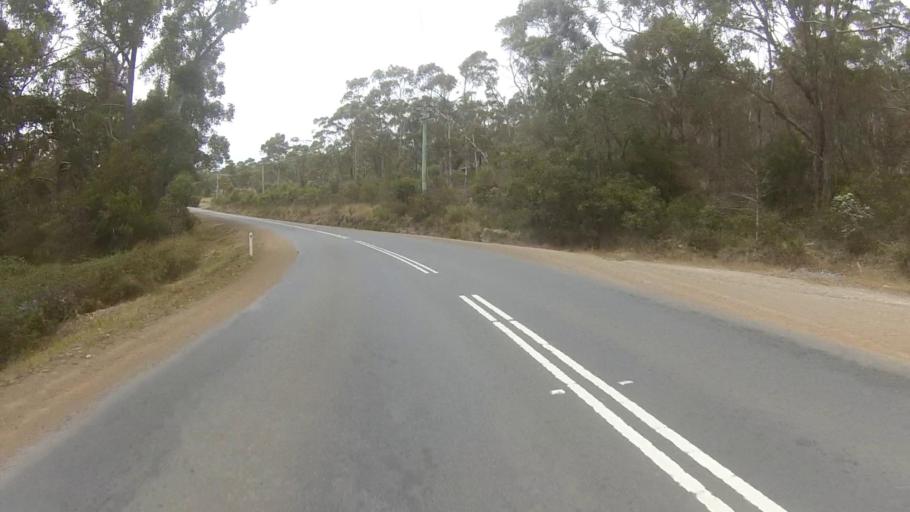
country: AU
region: Tasmania
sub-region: Kingborough
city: Margate
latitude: -43.0002
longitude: 147.2305
